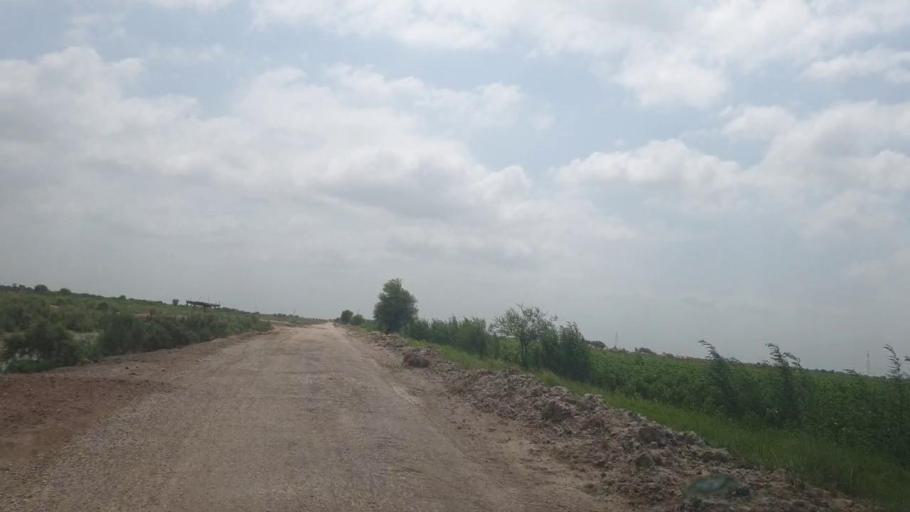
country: PK
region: Sindh
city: Tando Mittha Khan
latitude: 25.8871
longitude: 69.1594
